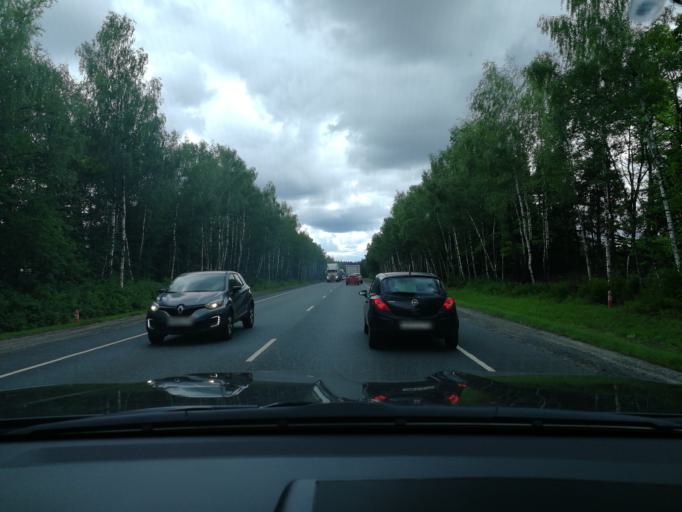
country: RU
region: Moskovskaya
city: Popovo
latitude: 55.0700
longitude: 37.8049
